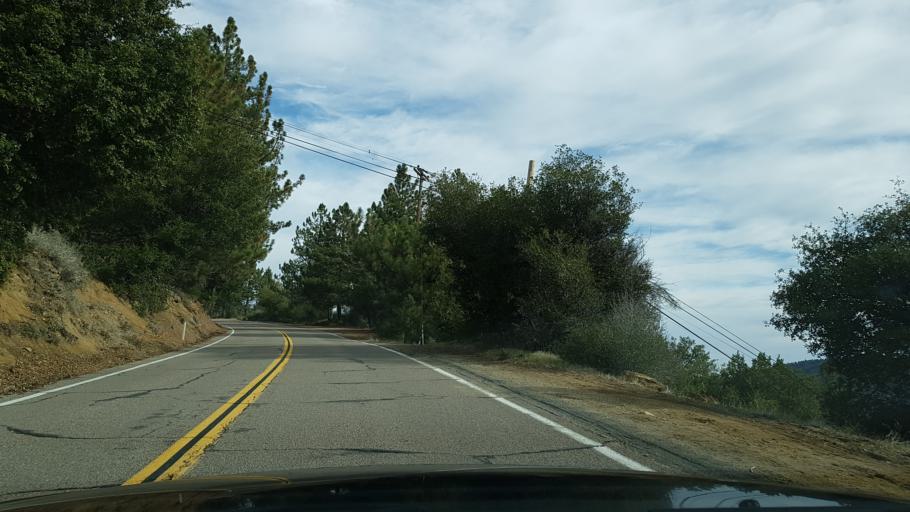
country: US
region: California
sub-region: Riverside County
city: Aguanga
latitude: 33.3445
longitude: -116.8748
